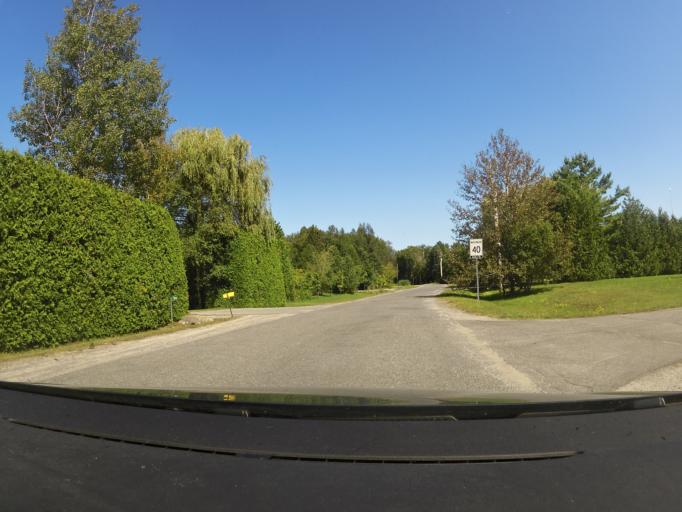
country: CA
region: Ontario
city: Bells Corners
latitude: 45.2907
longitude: -75.9914
